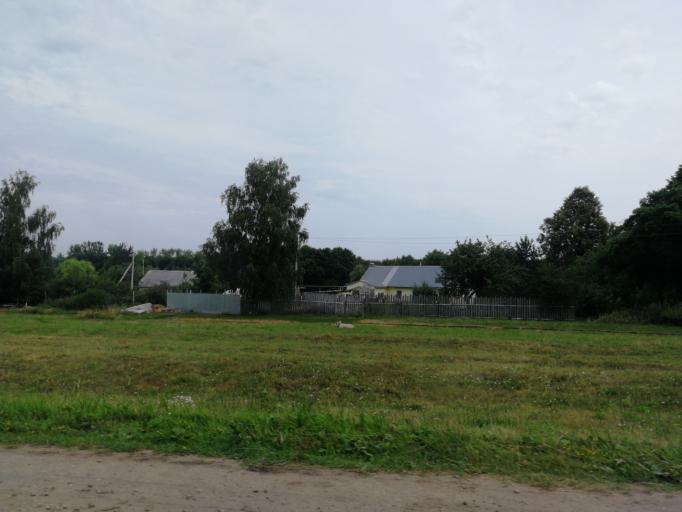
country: RU
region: Tula
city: Zhdankovskiy
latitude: 53.7114
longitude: 38.1427
